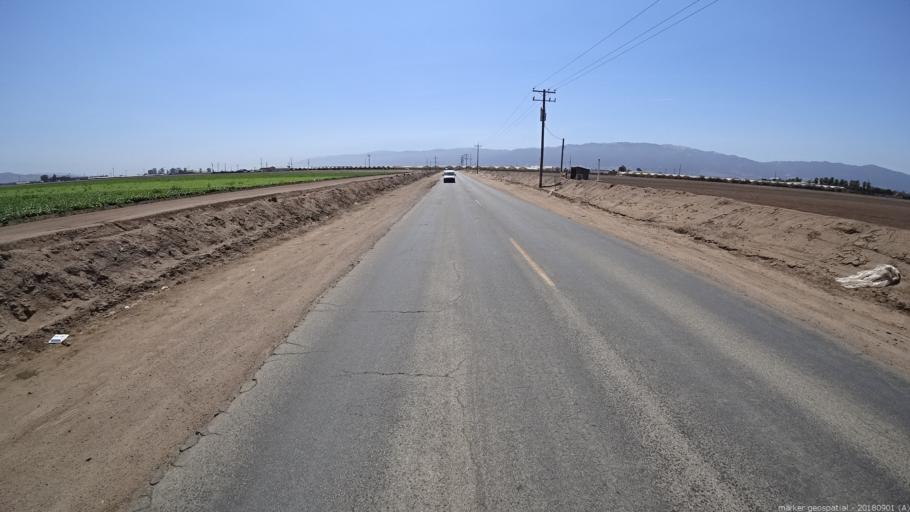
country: US
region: California
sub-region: Monterey County
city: Chualar
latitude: 36.6341
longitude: -121.5426
